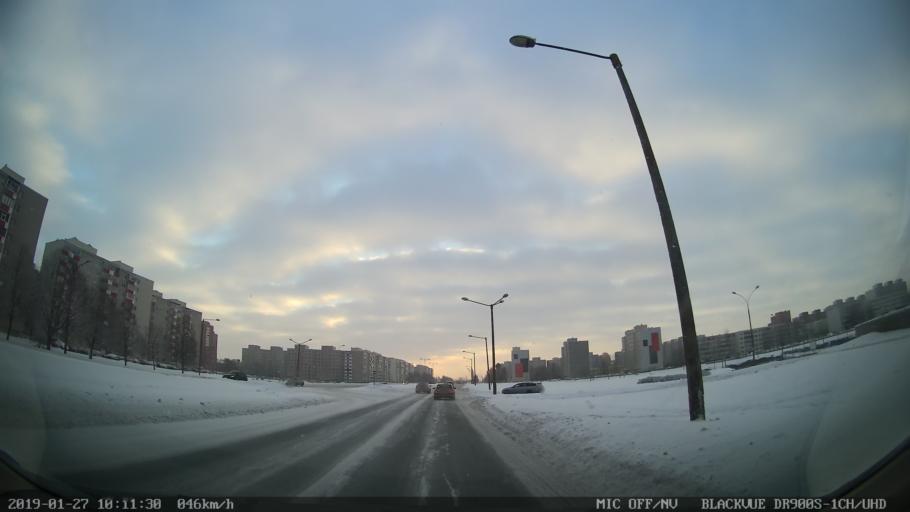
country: EE
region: Harju
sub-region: Tallinna linn
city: Kose
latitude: 59.4408
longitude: 24.8240
